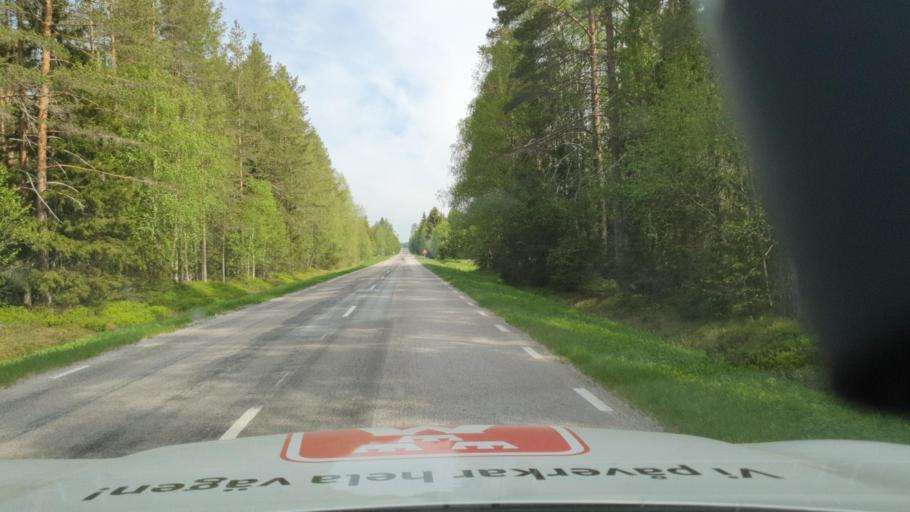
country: SE
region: Vaesterbotten
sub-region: Umea Kommun
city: Hoernefors
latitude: 63.6901
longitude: 19.9202
